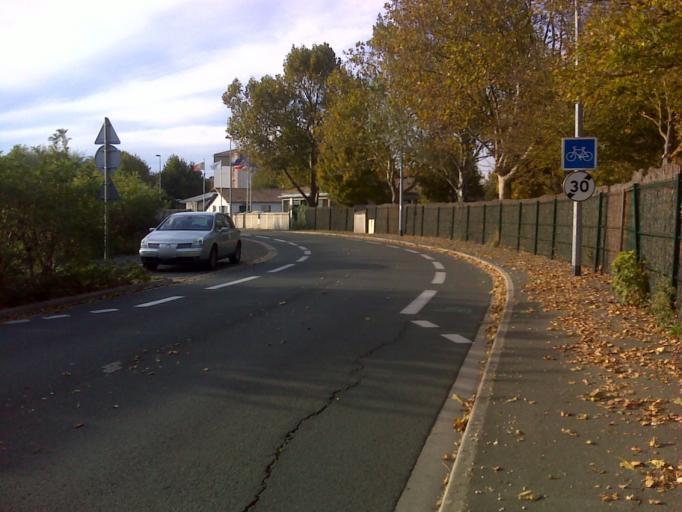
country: FR
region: Poitou-Charentes
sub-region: Departement de la Charente-Maritime
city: Rochefort
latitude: 45.9298
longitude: -0.9574
